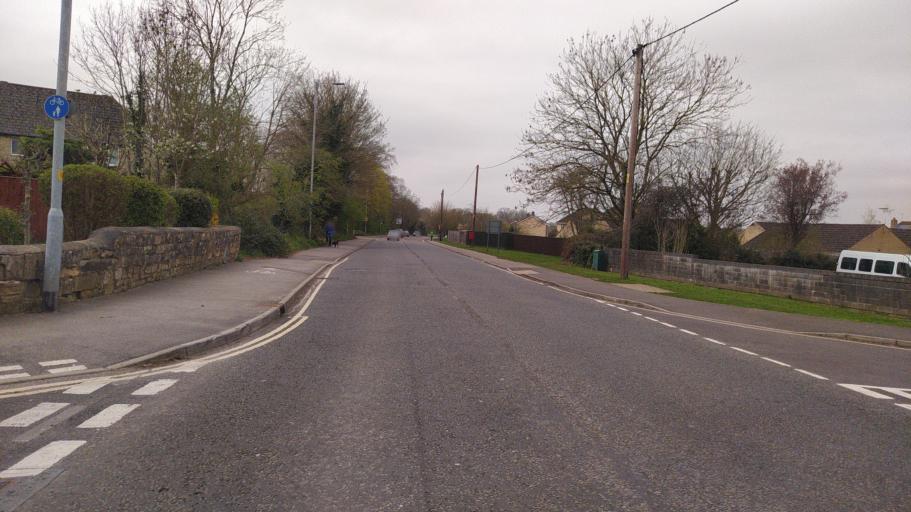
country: GB
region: England
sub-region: Wiltshire
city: Trowbridge
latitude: 51.3162
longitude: -2.2249
